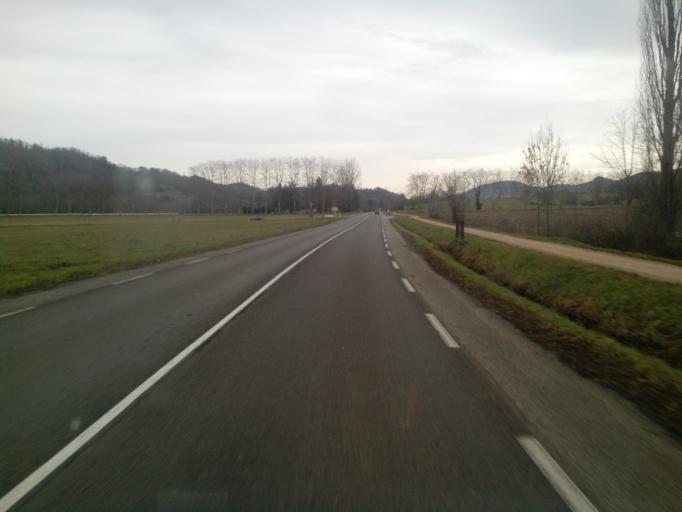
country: FR
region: Midi-Pyrenees
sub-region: Departement de l'Ariege
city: Foix
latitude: 43.0179
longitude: 1.3912
